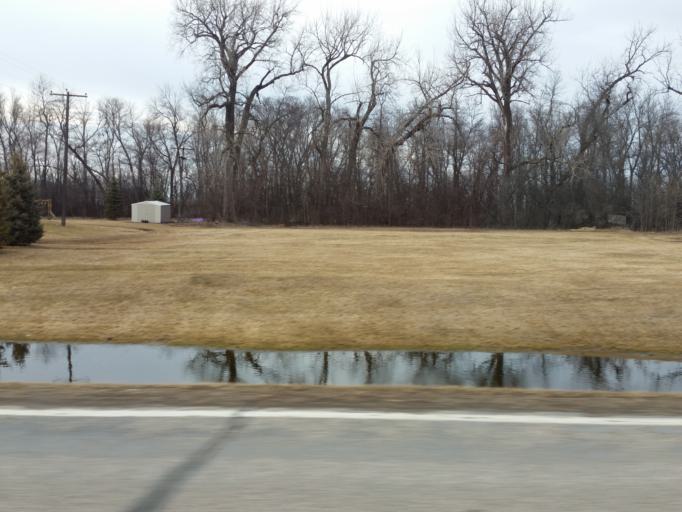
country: US
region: North Dakota
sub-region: Cass County
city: Casselton
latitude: 47.0065
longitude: -97.2174
